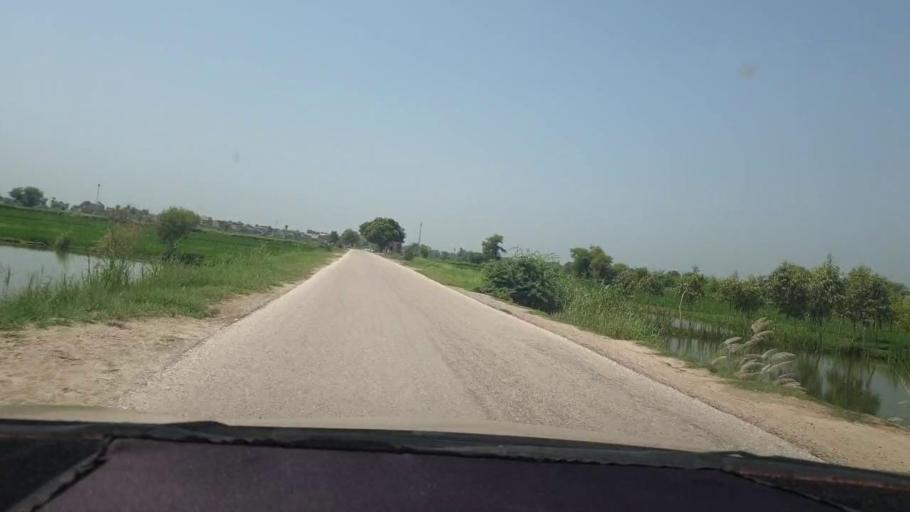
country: PK
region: Sindh
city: Kambar
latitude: 27.6172
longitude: 68.0594
